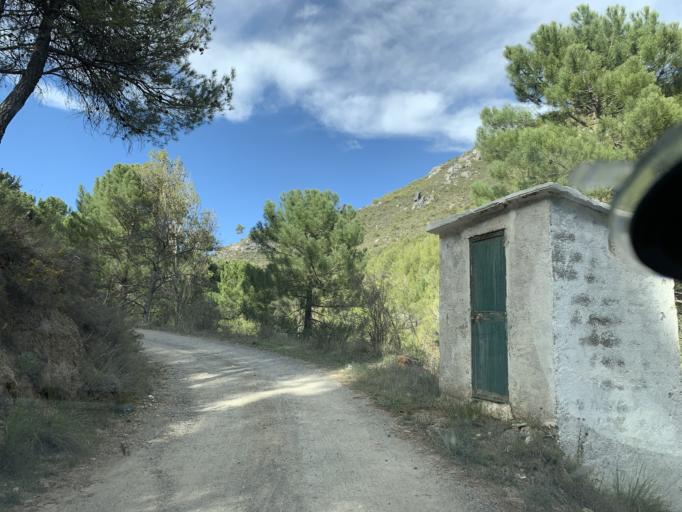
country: ES
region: Andalusia
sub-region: Provincia de Granada
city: Quentar
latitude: 37.2266
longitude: -3.4094
